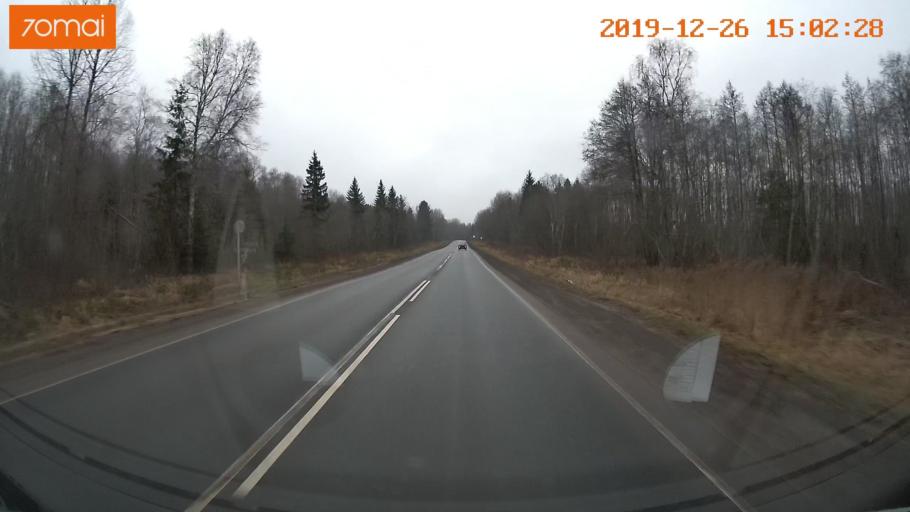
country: RU
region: Jaroslavl
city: Rybinsk
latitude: 58.2249
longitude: 38.8748
